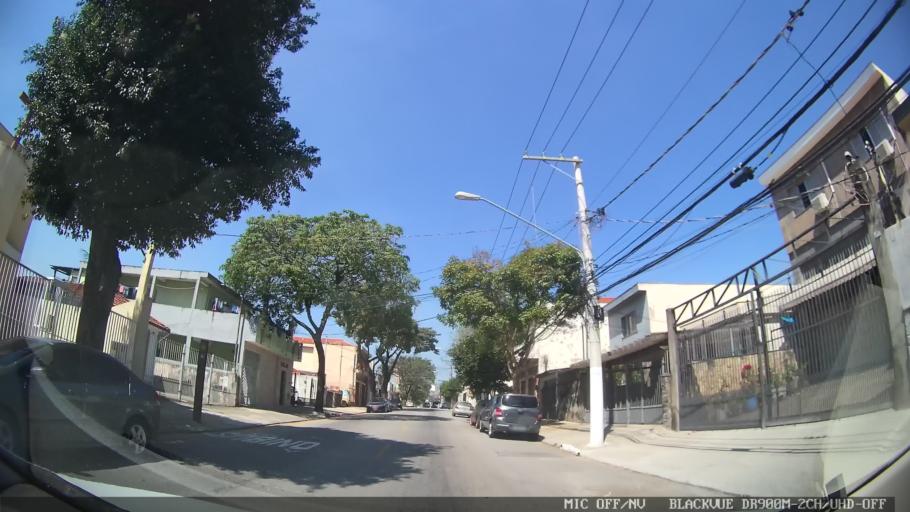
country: BR
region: Sao Paulo
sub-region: Sao Paulo
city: Sao Paulo
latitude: -23.4950
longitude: -46.6535
